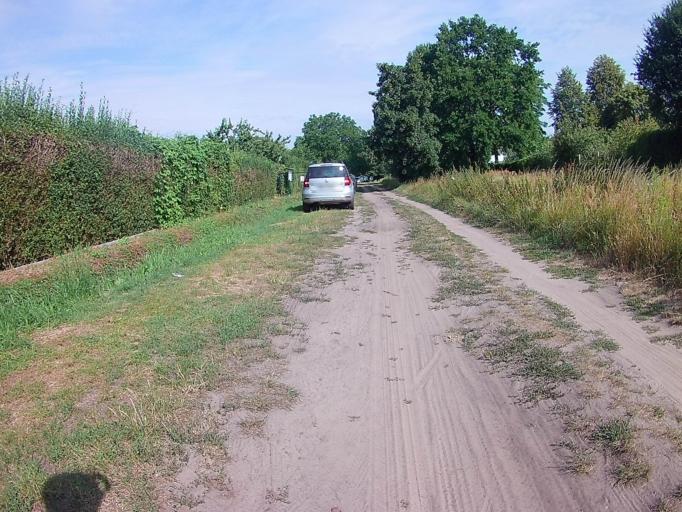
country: DE
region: Berlin
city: Adlershof
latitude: 52.4208
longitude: 13.5484
